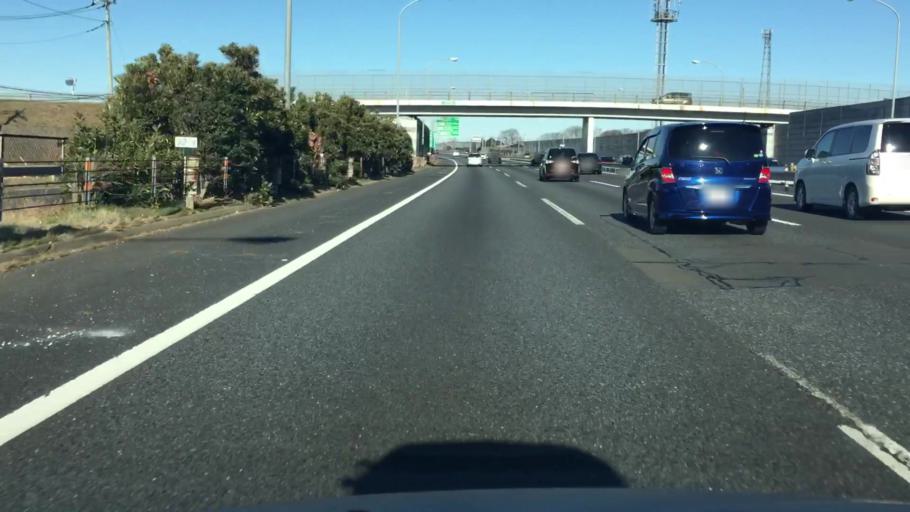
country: JP
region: Saitama
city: Kawagoe
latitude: 35.9037
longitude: 139.4522
